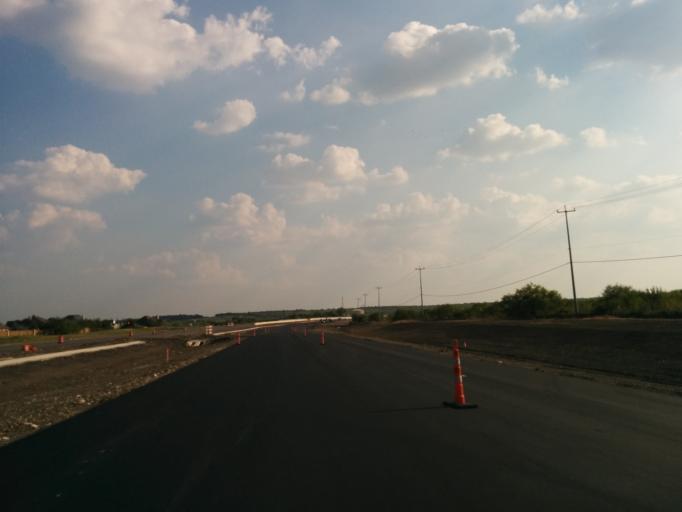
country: US
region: Texas
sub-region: Bexar County
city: Converse
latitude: 29.4906
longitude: -98.2908
